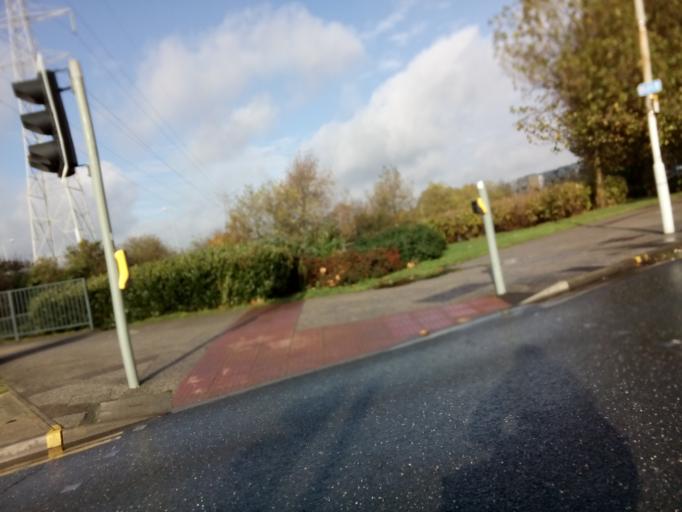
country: GB
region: England
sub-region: Suffolk
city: Ipswich
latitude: 52.0578
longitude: 1.1349
